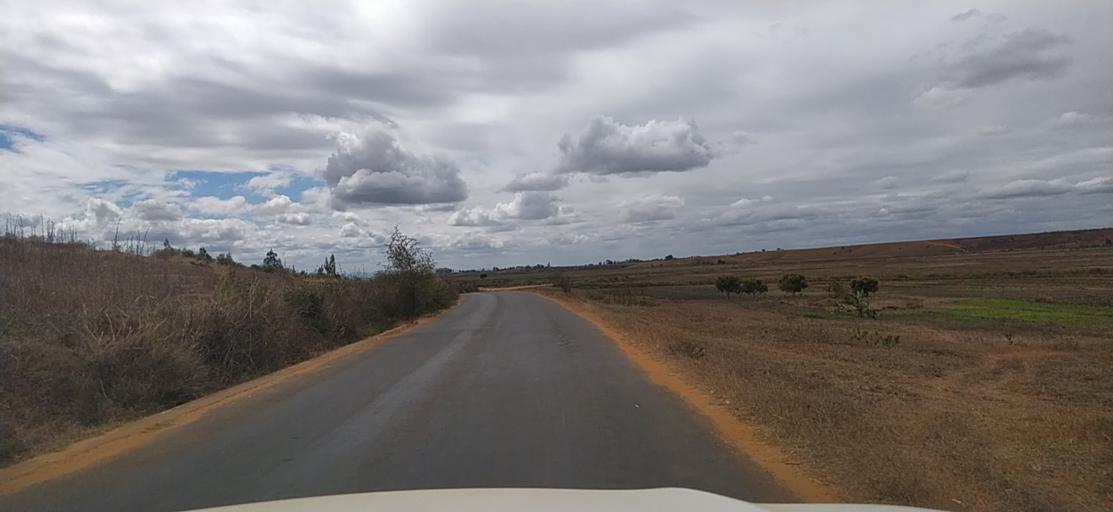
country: MG
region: Alaotra Mangoro
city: Ambatondrazaka
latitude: -17.9239
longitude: 48.2581
